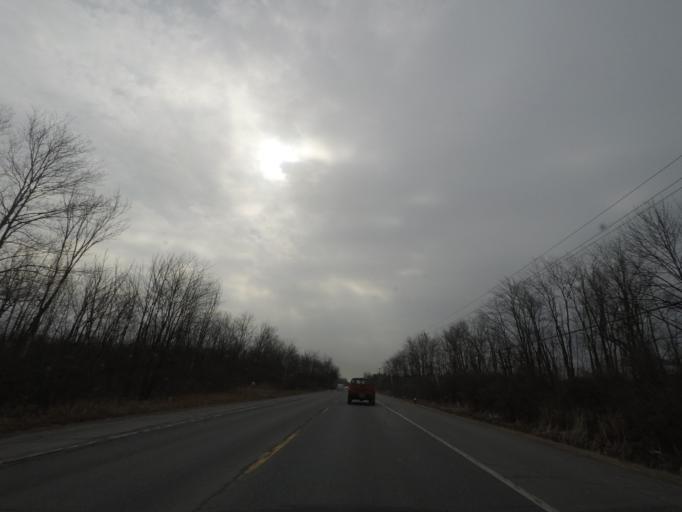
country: US
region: New York
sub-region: Warren County
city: Glens Falls
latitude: 43.3278
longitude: -73.6289
